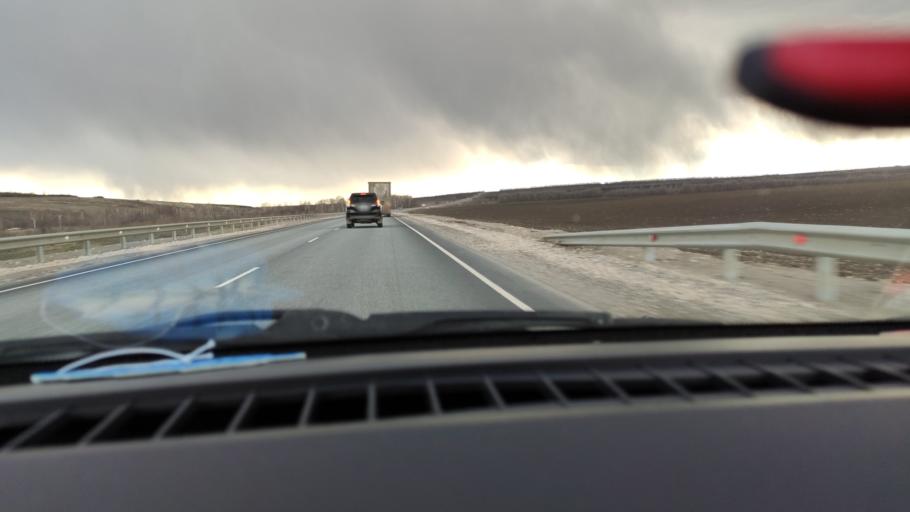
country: RU
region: Saratov
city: Yelshanka
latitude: 51.8565
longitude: 46.4947
